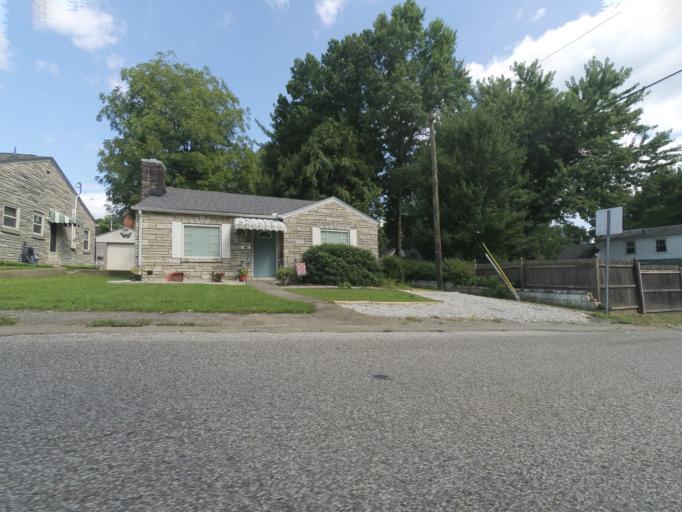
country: US
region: West Virginia
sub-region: Cabell County
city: Huntington
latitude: 38.4074
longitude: -82.4266
